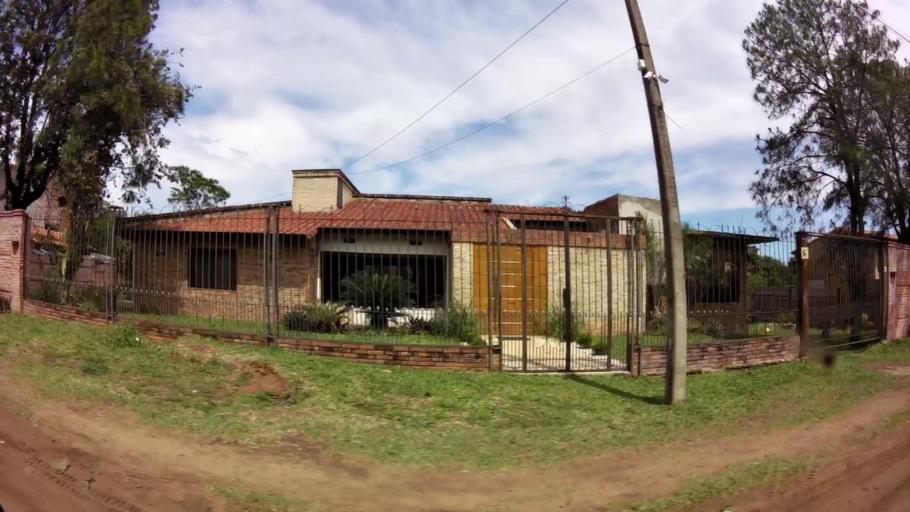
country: PY
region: Central
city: Limpio
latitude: -25.1633
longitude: -57.4779
